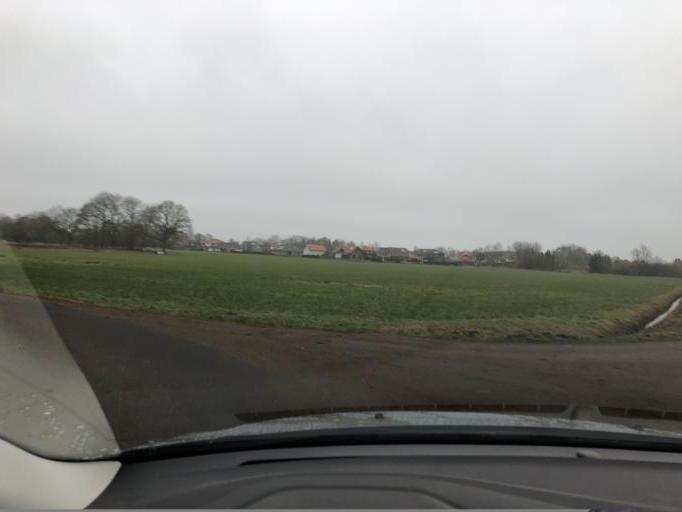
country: DE
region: Lower Saxony
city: Bad Zwischenahn
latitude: 53.1709
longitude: 8.0158
